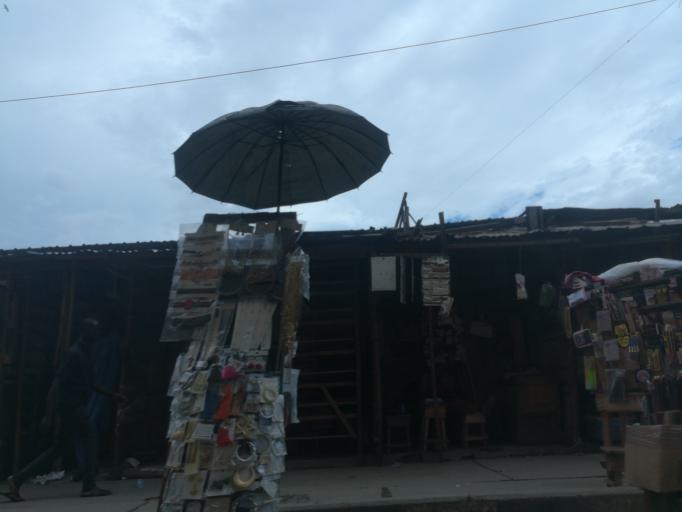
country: NG
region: Lagos
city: Lagos
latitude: 6.4565
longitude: 3.3860
